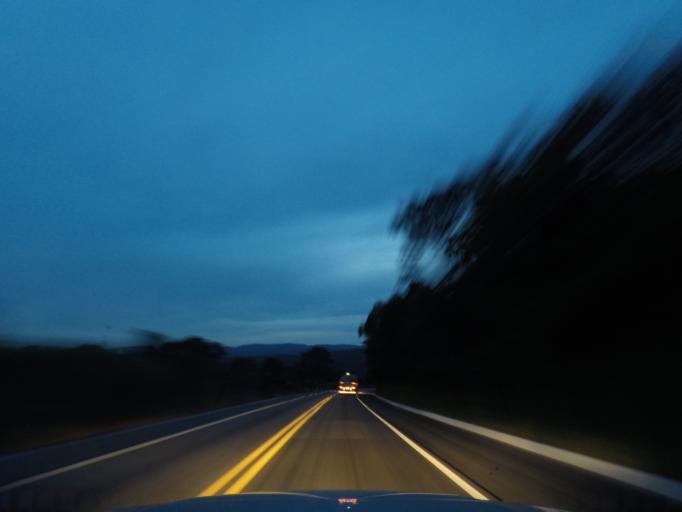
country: BR
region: Bahia
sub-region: Andarai
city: Vera Cruz
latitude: -12.4953
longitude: -41.3211
